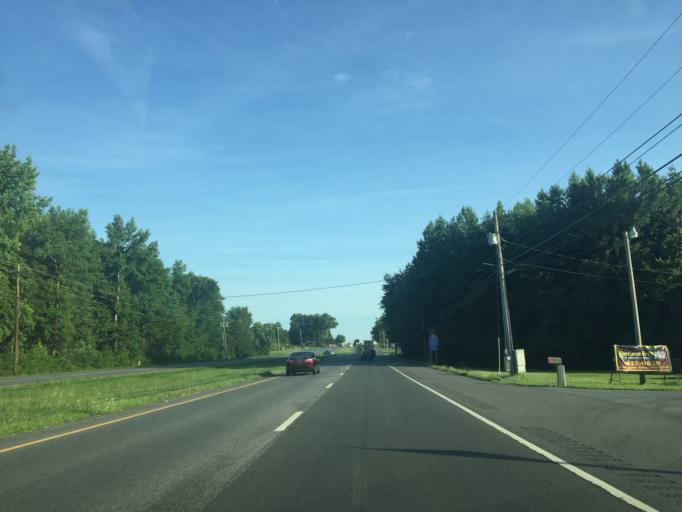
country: US
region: Delaware
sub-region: Kent County
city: Cheswold
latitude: 39.2605
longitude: -75.5865
